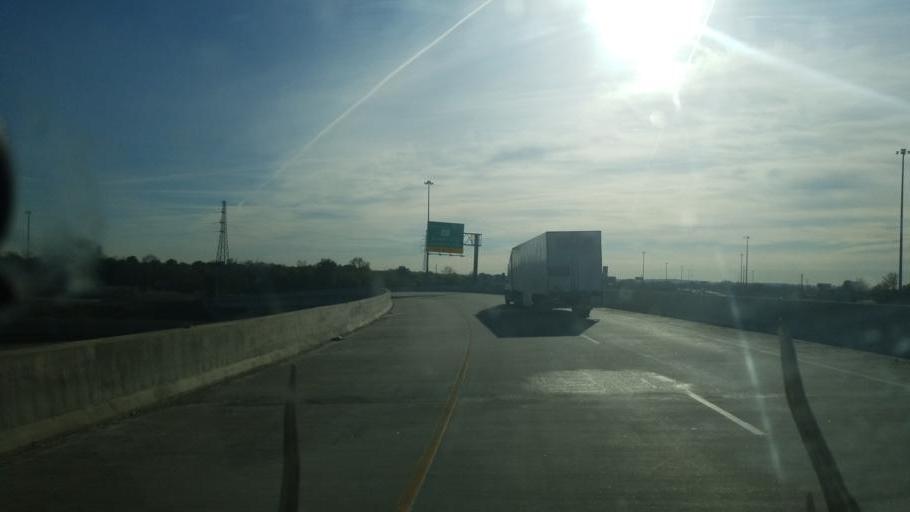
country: US
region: Illinois
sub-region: Saint Clair County
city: East Saint Louis
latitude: 38.6333
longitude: -90.1456
